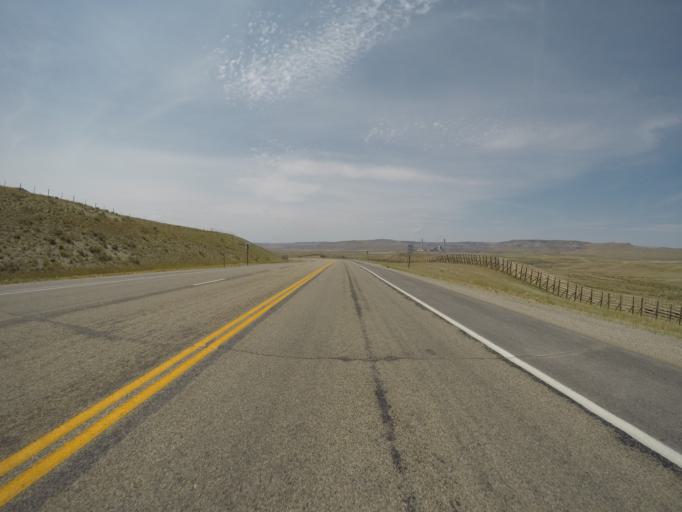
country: US
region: Wyoming
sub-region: Lincoln County
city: Kemmerer
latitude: 41.7694
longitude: -110.5556
